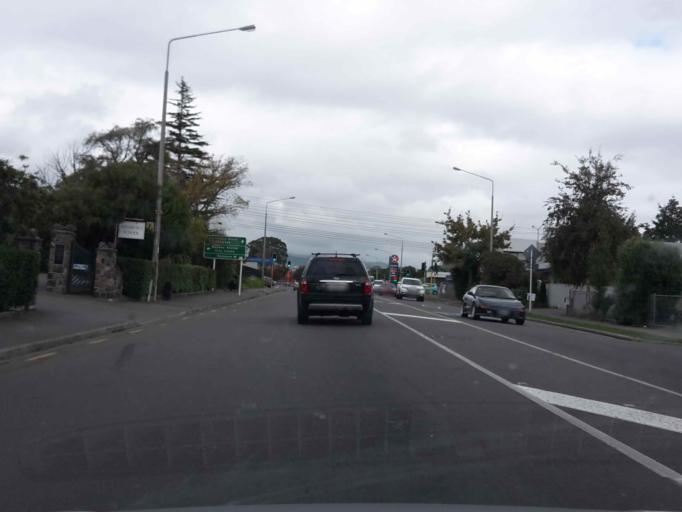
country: NZ
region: Canterbury
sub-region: Christchurch City
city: Christchurch
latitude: -43.5364
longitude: 172.5965
